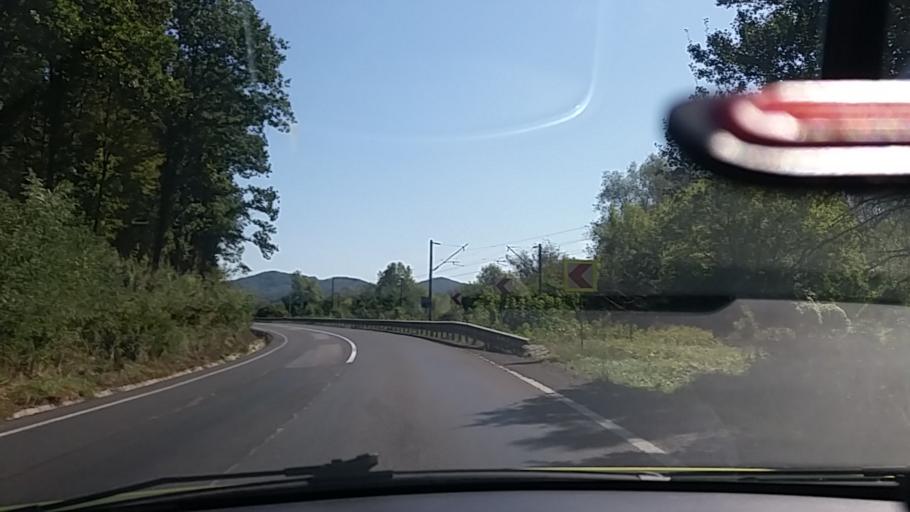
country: RO
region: Hunedoara
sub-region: Comuna Zam
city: Zam
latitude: 46.0136
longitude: 22.4265
